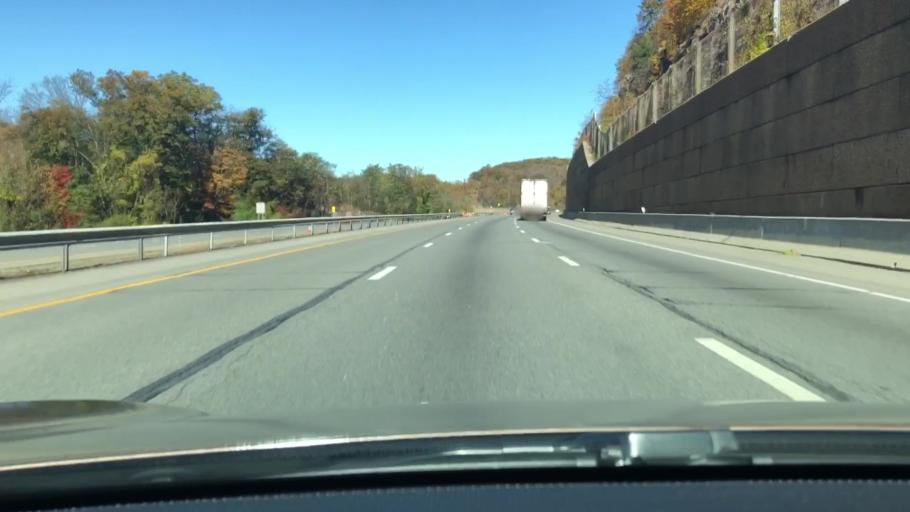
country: US
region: New York
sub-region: Rockland County
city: Sloatsburg
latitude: 41.1961
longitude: -74.1819
